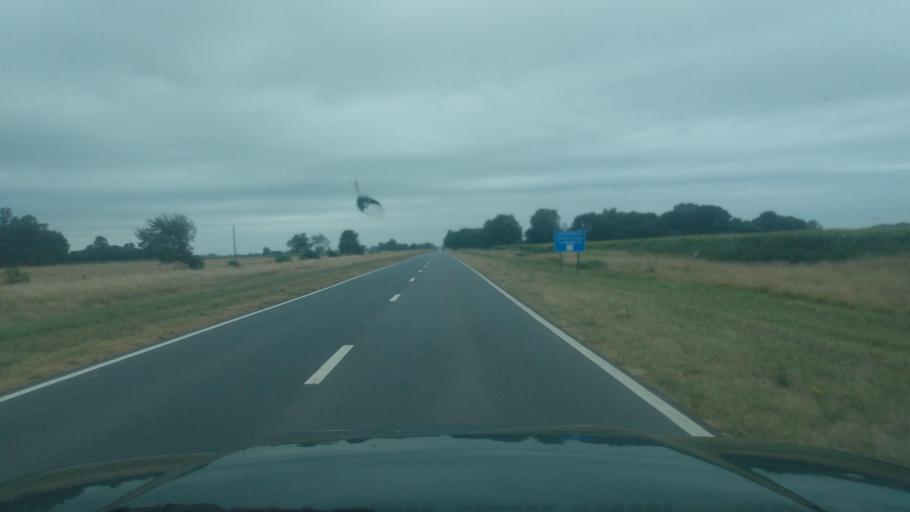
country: AR
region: Buenos Aires
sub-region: Partido de Bragado
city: Bragado
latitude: -35.2999
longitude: -60.6137
